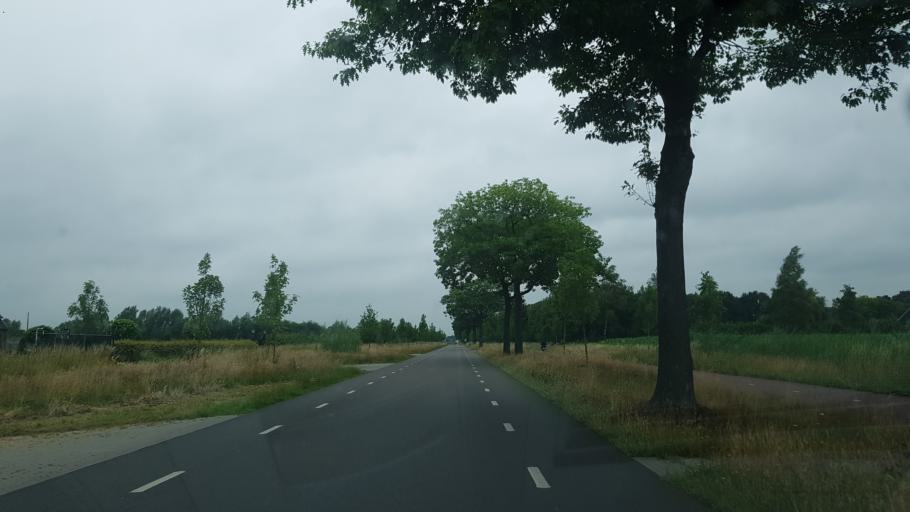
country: NL
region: North Brabant
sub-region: Gemeente Son en Breugel
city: Son
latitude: 51.5390
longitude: 5.4860
